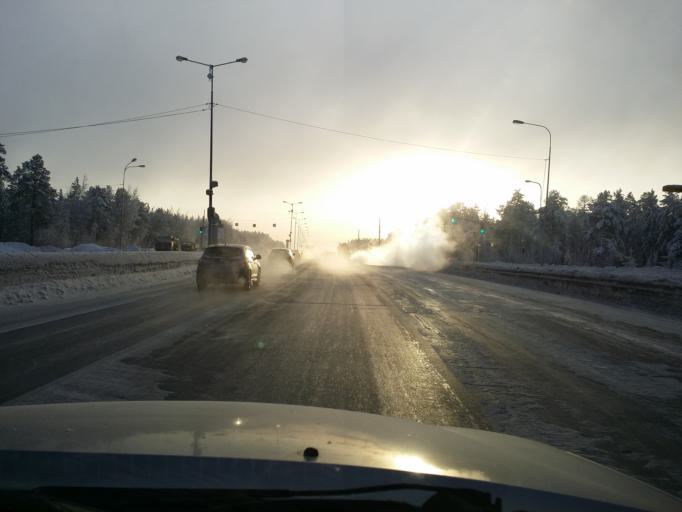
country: RU
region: Khanty-Mansiyskiy Avtonomnyy Okrug
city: Surgut
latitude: 61.3174
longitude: 73.3924
